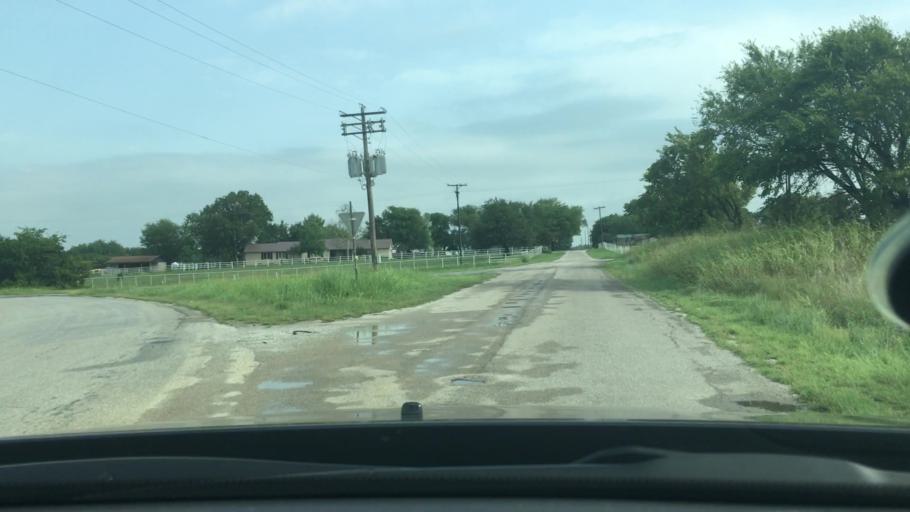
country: US
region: Oklahoma
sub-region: Carter County
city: Lone Grove
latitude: 34.2156
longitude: -97.2650
